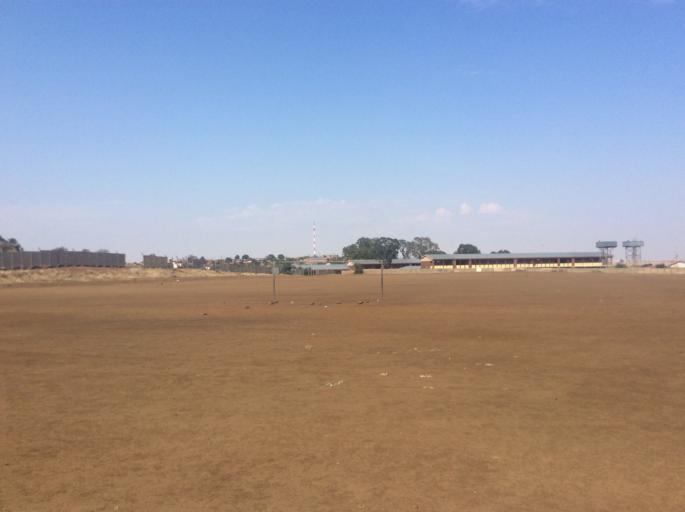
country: LS
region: Mafeteng
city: Mafeteng
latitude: -29.7148
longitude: 27.0316
